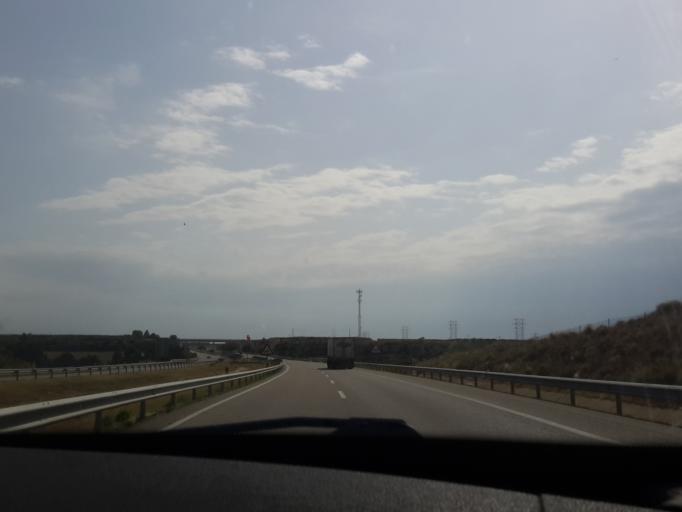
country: ES
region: Catalonia
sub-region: Provincia de Lleida
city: Sunyer
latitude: 41.5520
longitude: 0.5872
